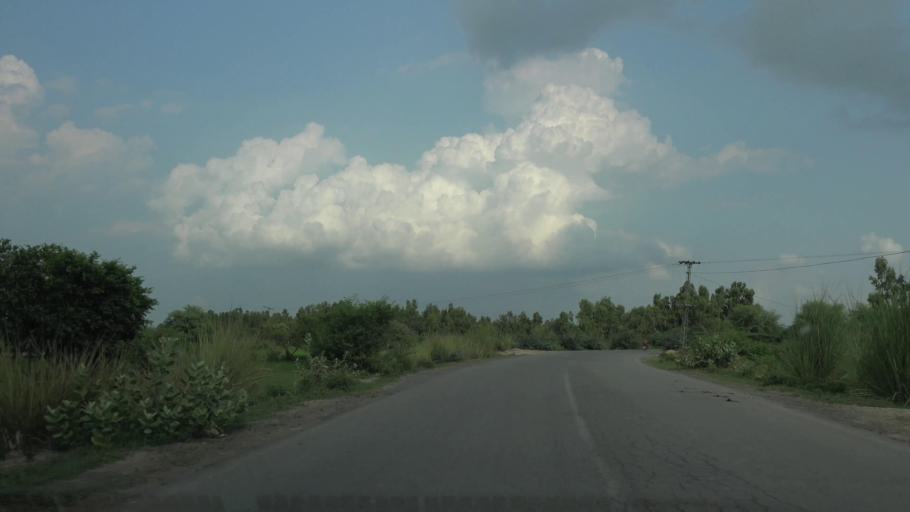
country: PK
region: Punjab
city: Nankana Sahib
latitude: 31.4944
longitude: 73.6024
